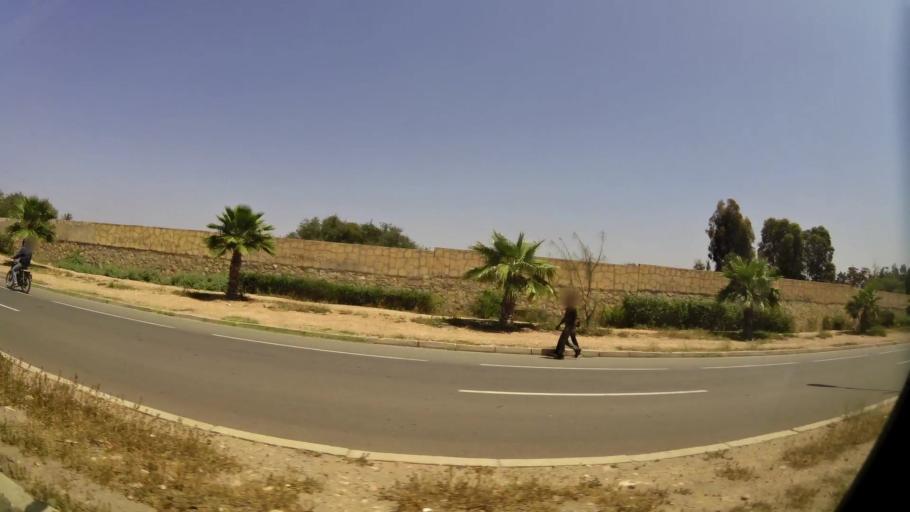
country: MA
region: Souss-Massa-Draa
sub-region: Inezgane-Ait Mellou
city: Inezgane
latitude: 30.3525
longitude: -9.4875
